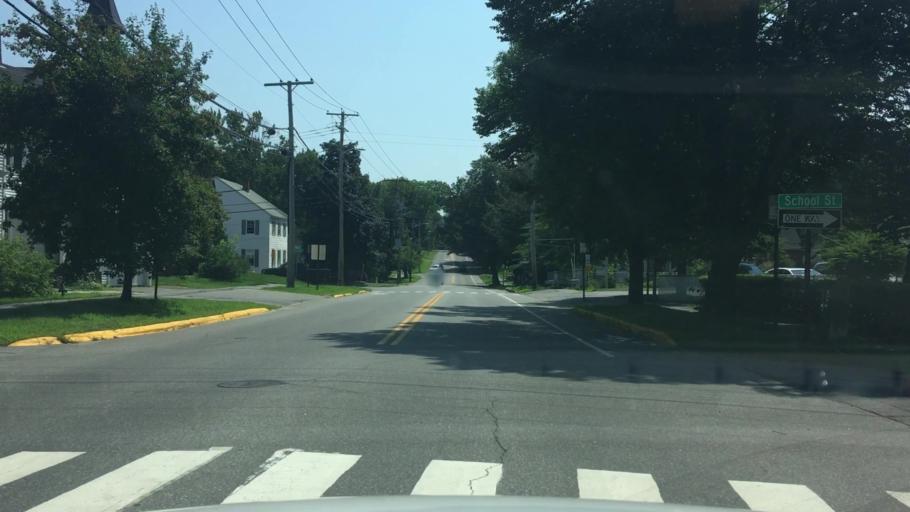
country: US
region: Maine
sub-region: Cumberland County
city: Brunswick
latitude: 43.9147
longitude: -69.9625
